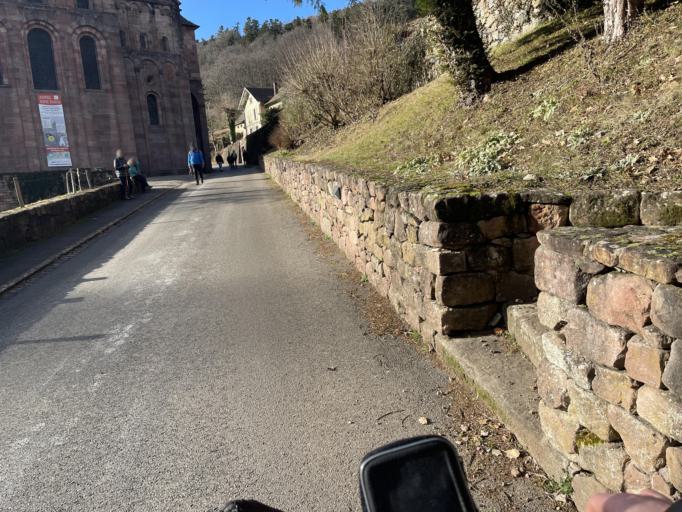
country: FR
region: Alsace
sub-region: Departement du Haut-Rhin
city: Lautenbach
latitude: 47.9234
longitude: 7.1586
